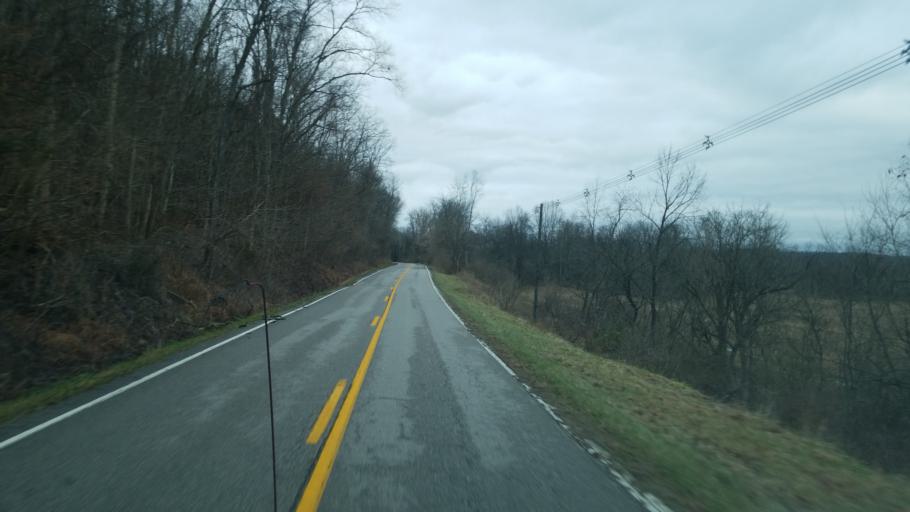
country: US
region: Ohio
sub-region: Clermont County
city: New Richmond
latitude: 38.9016
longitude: -84.2567
